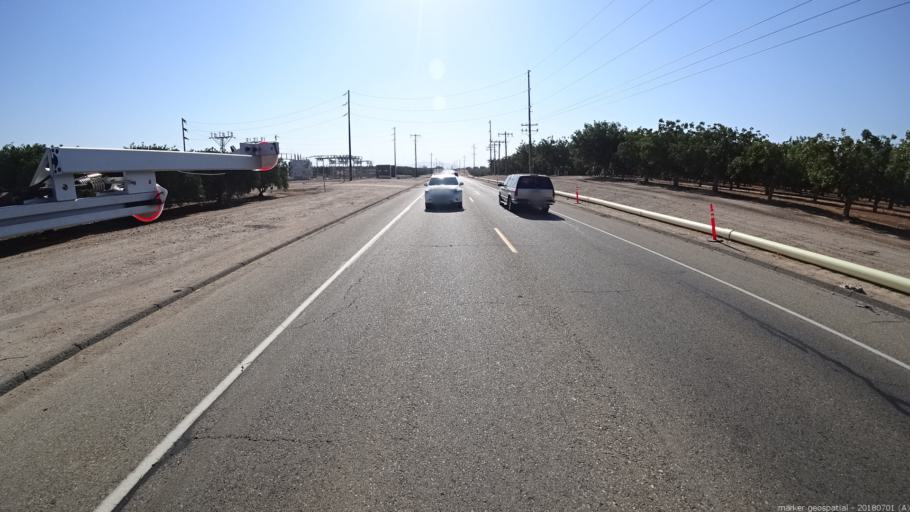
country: US
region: California
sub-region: Madera County
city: Bonadelle Ranchos-Madera Ranchos
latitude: 36.9232
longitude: -119.8134
